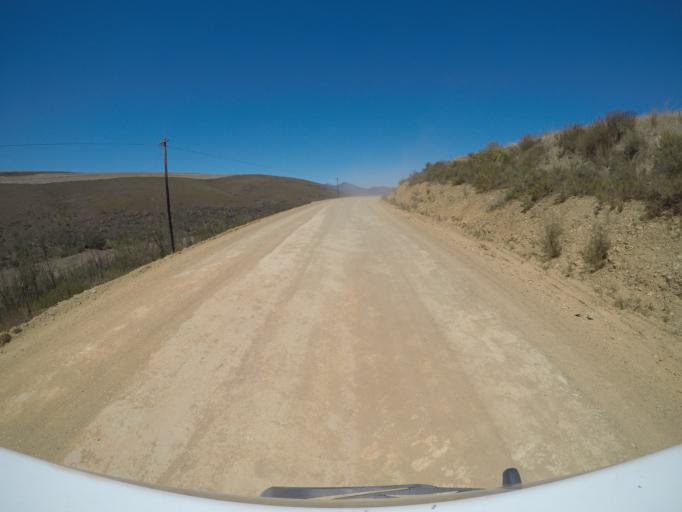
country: ZA
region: Western Cape
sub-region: Overberg District Municipality
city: Grabouw
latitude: -34.2144
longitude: 19.2097
